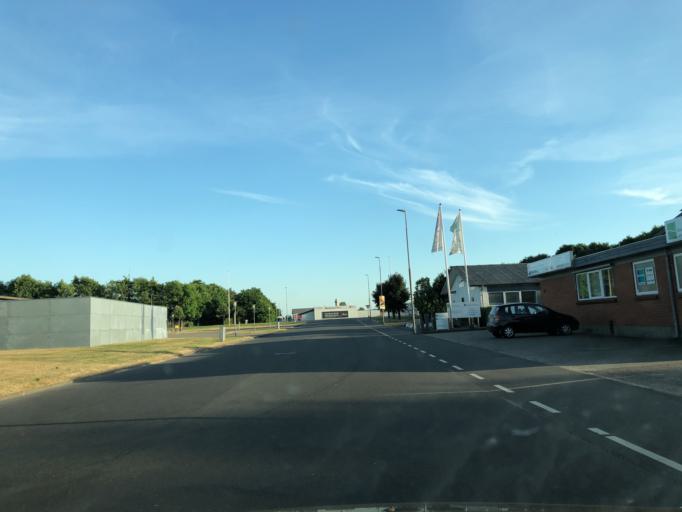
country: DK
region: Central Jutland
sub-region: Struer Kommune
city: Struer
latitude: 56.4818
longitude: 8.5769
